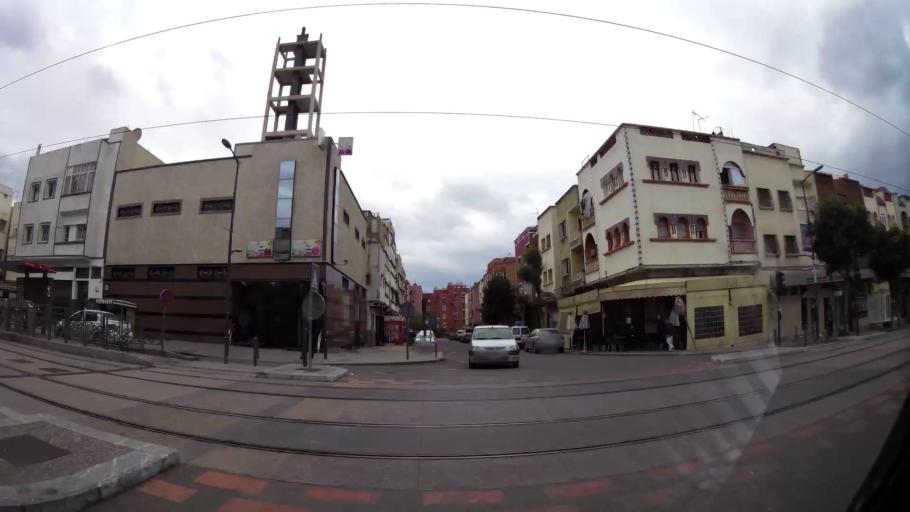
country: MA
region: Grand Casablanca
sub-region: Casablanca
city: Casablanca
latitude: 33.5893
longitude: -7.5680
